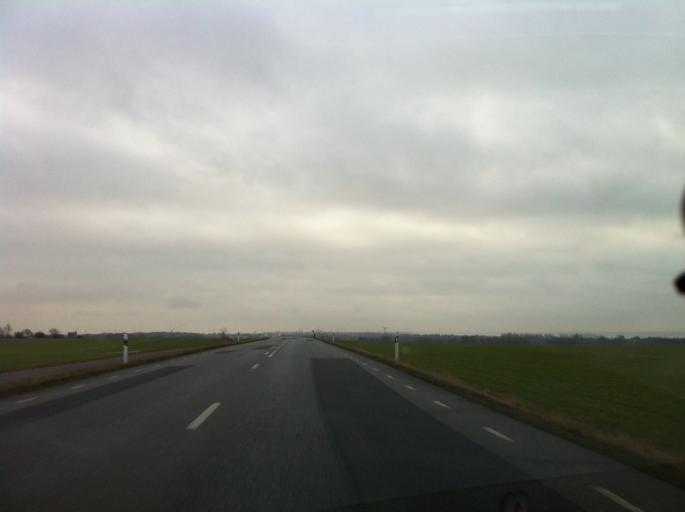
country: SE
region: Skane
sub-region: Helsingborg
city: Glumslov
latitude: 55.9212
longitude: 12.8157
